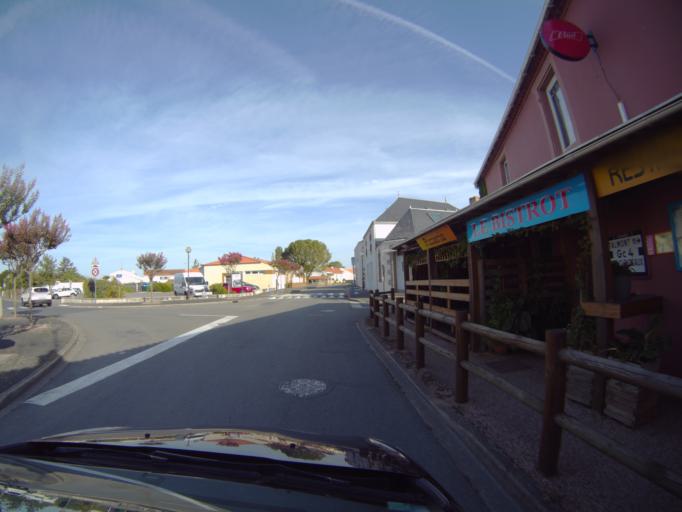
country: FR
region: Pays de la Loire
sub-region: Departement de la Vendee
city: Nieul-le-Dolent
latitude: 46.5753
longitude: -1.5102
